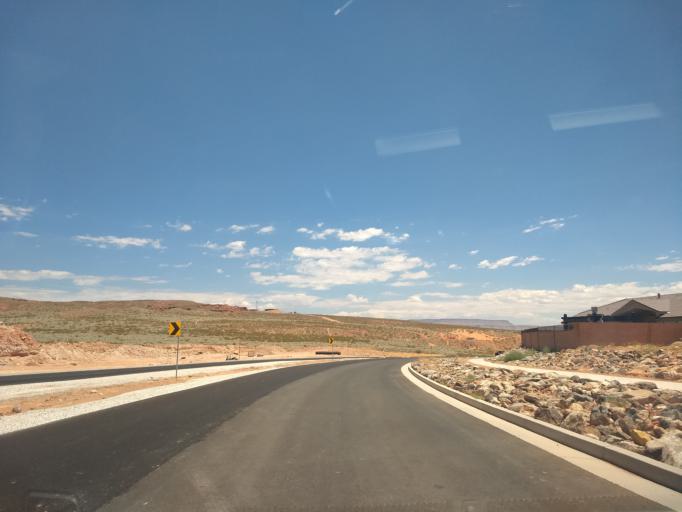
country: US
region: Utah
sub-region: Washington County
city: Washington
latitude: 37.1595
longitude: -113.5217
